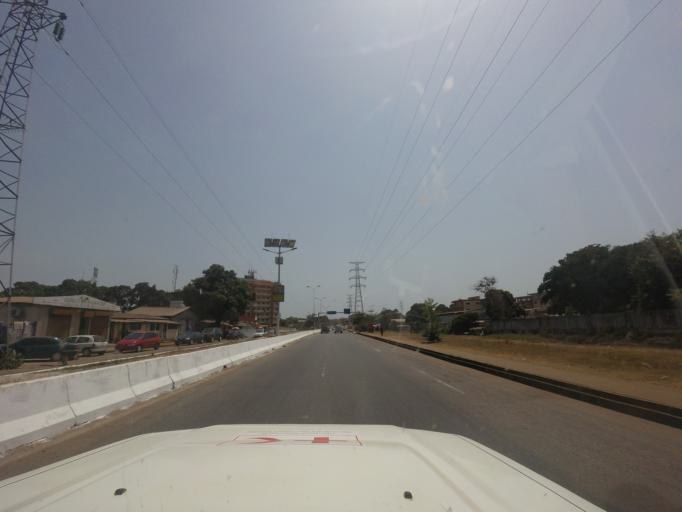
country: GN
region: Conakry
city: Camayenne
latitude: 9.5280
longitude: -13.6862
